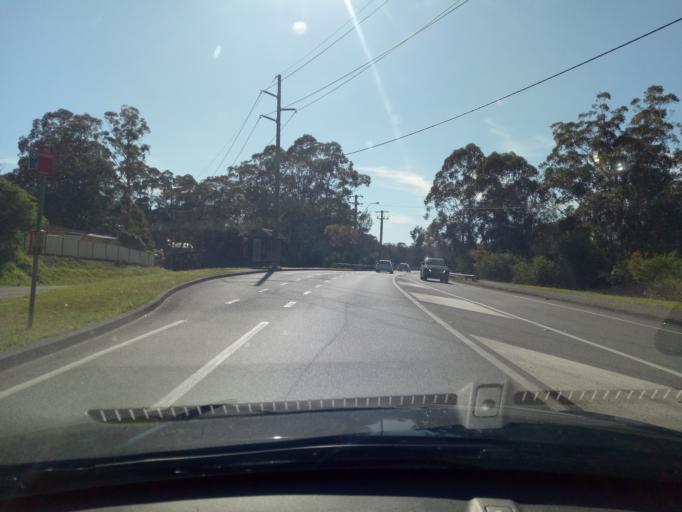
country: AU
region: New South Wales
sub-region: Gosford Shire
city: Erina
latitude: -33.4330
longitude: 151.3810
